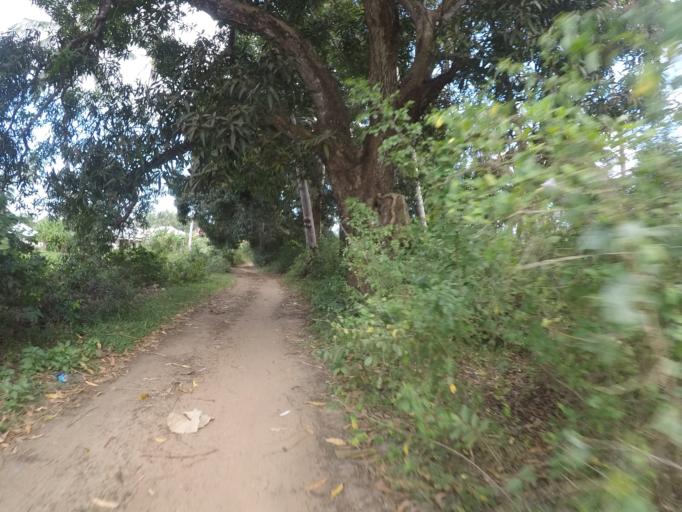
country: TZ
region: Zanzibar Urban/West
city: Zanzibar
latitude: -6.2059
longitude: 39.2352
